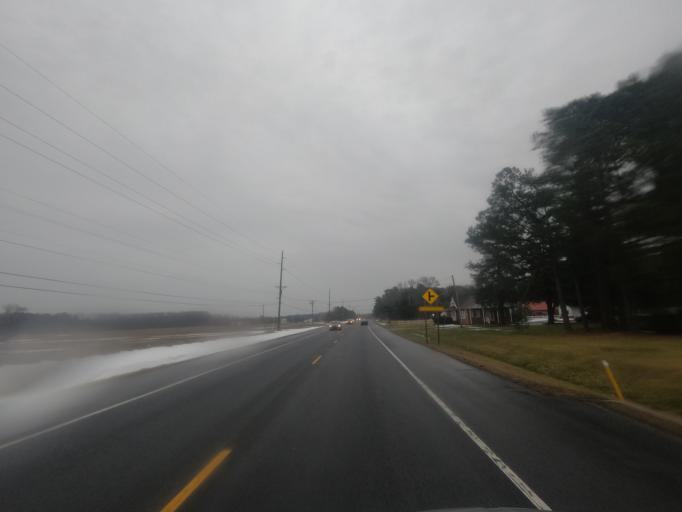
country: US
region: Maryland
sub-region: Dorchester County
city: Cambridge
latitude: 38.5582
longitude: -75.9991
